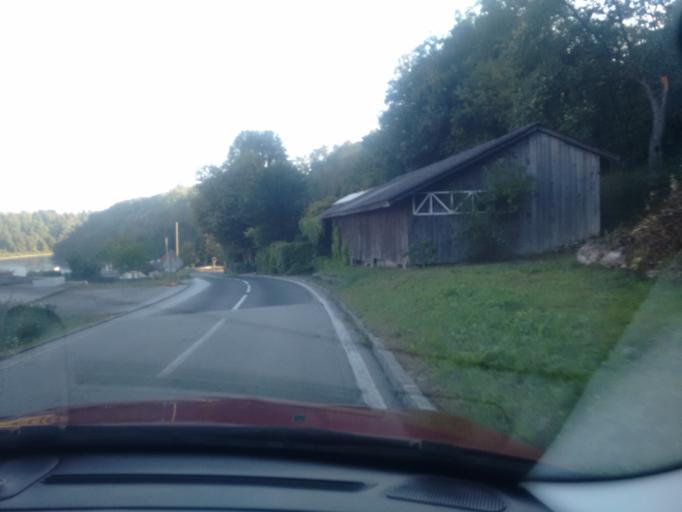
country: DE
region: Bavaria
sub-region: Upper Bavaria
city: Burghausen
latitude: 48.1557
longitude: 12.8345
